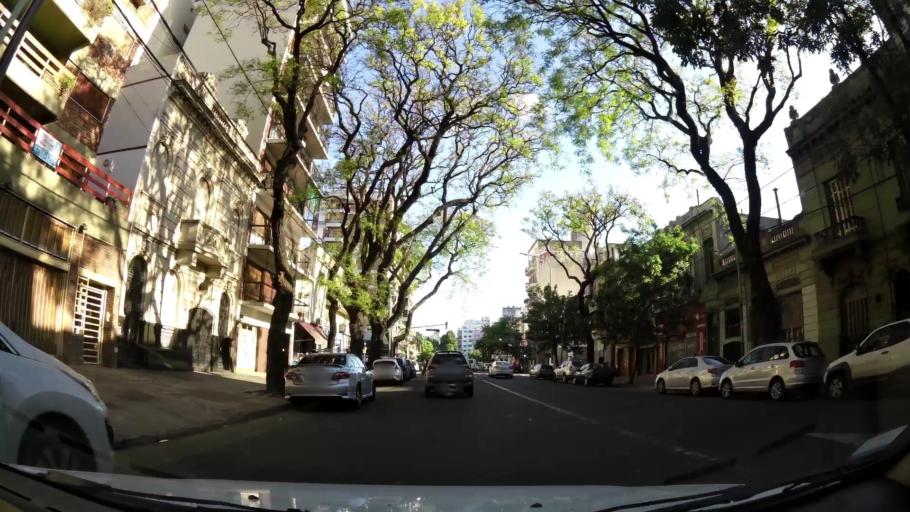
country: AR
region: Buenos Aires F.D.
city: Buenos Aires
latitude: -34.6153
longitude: -58.4202
